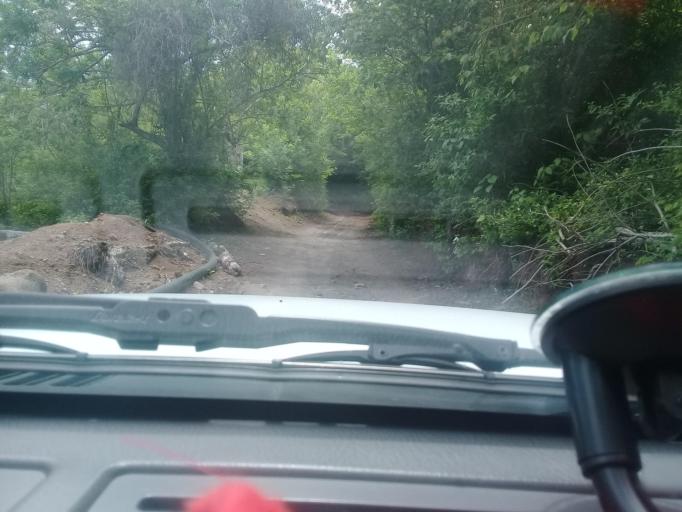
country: MX
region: Veracruz
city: Paso de Ovejas
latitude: 19.2841
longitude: -96.4290
